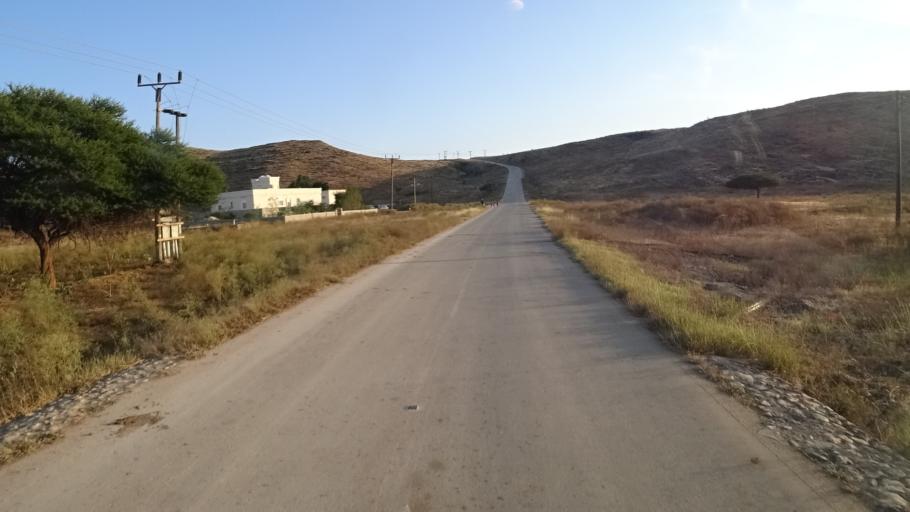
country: OM
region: Zufar
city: Salalah
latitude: 17.1532
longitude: 54.6183
